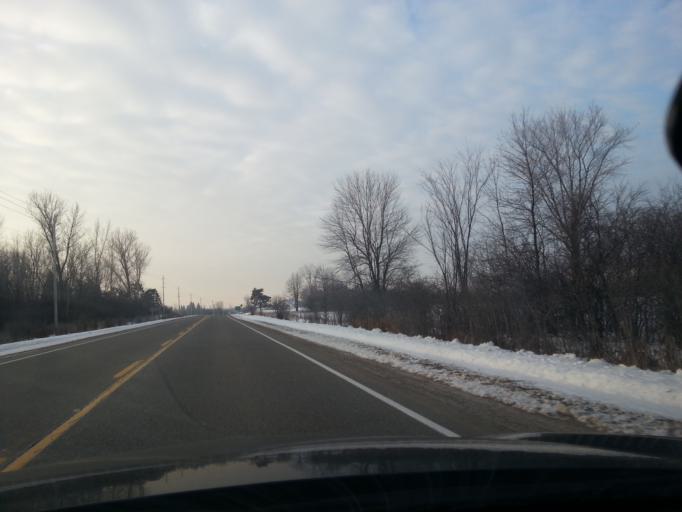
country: CA
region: Ontario
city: Perth
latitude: 44.9406
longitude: -76.2393
